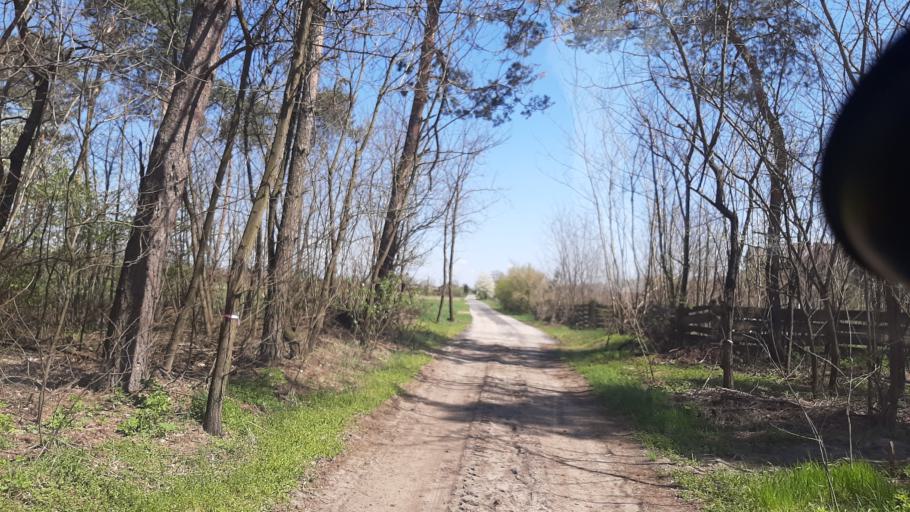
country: PL
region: Lublin Voivodeship
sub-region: Powiat lubelski
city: Garbow
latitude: 51.4031
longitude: 22.3185
